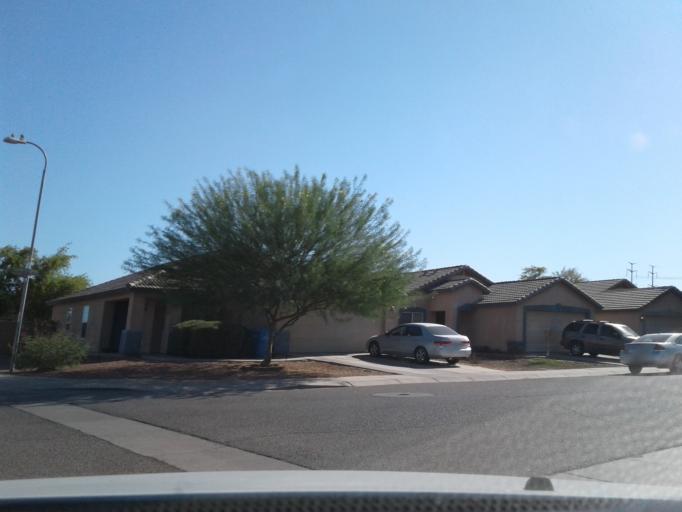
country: US
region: Arizona
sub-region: Maricopa County
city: Laveen
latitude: 33.4090
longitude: -112.1909
